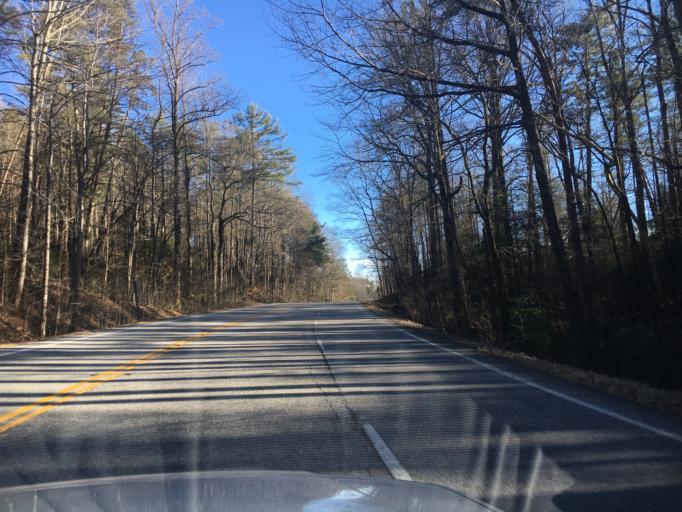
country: US
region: Georgia
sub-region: White County
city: Cleveland
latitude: 34.6905
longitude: -83.9095
